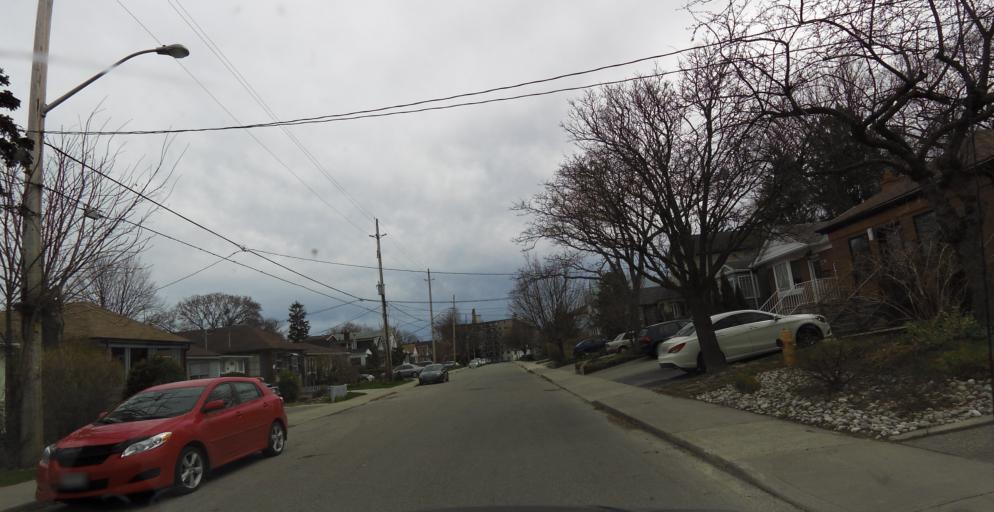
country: CA
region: Ontario
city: Etobicoke
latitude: 43.5964
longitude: -79.5107
